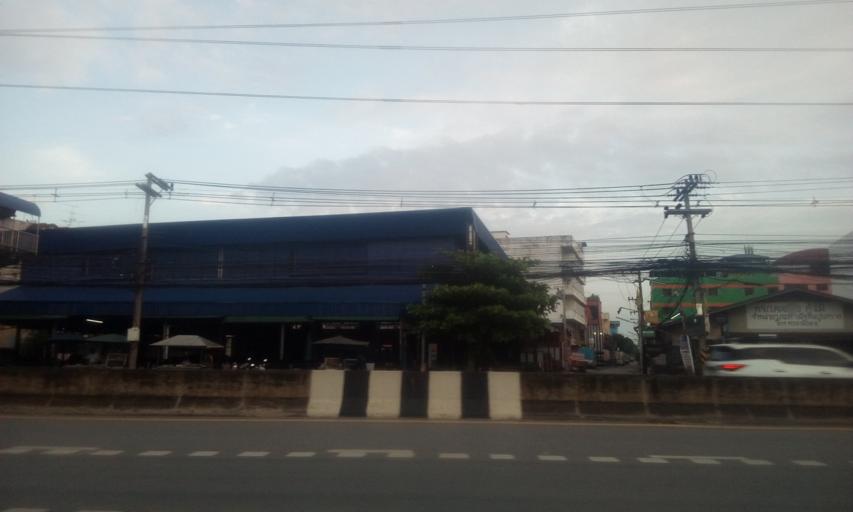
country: TH
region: Pathum Thani
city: Khlong Luang
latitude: 13.9932
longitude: 100.6551
